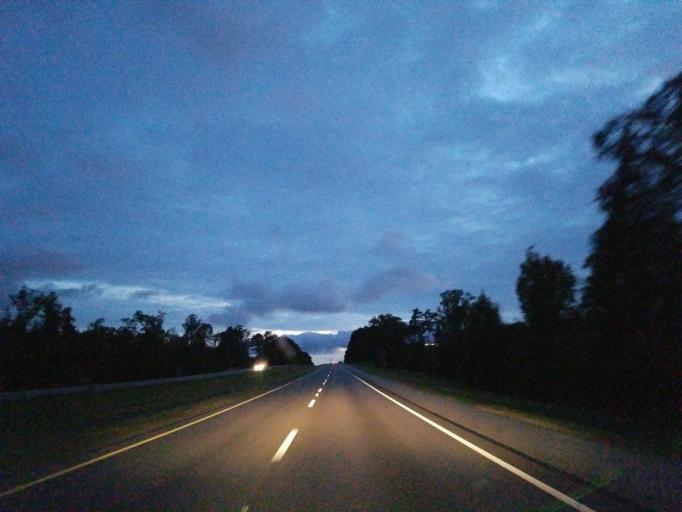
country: US
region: Mississippi
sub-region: Jones County
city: Sharon
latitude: 31.9368
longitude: -88.9928
